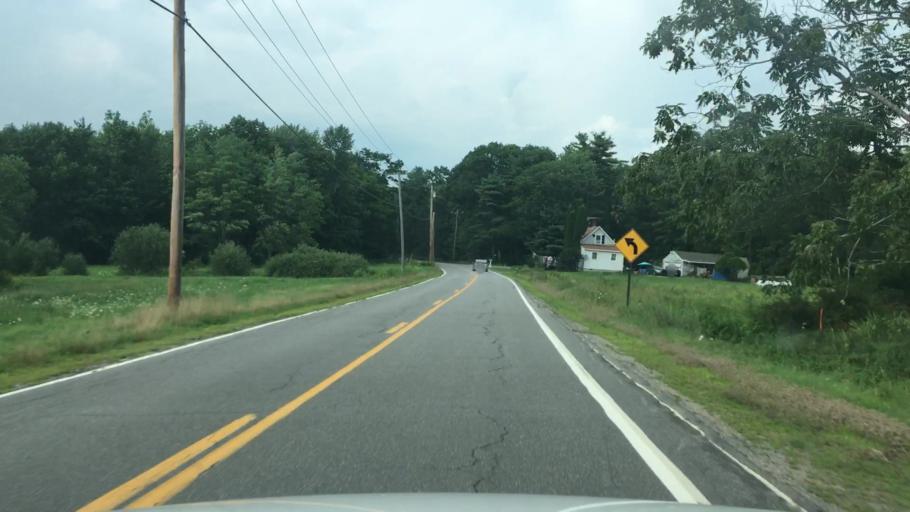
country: US
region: Maine
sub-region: Knox County
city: Washington
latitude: 44.2881
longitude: -69.3637
